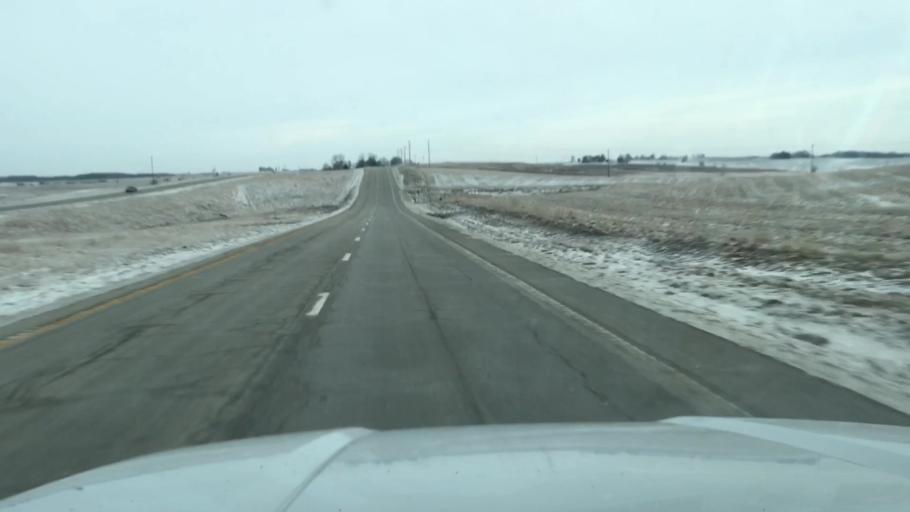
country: US
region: Missouri
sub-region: Andrew County
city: Savannah
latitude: 39.9781
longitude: -94.8770
